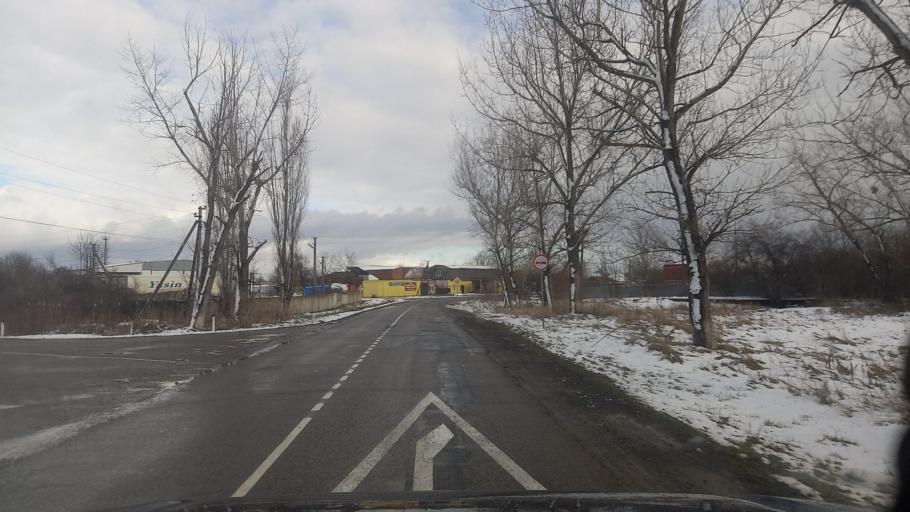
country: RU
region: Krasnodarskiy
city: Smolenskaya
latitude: 44.7763
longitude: 38.8323
